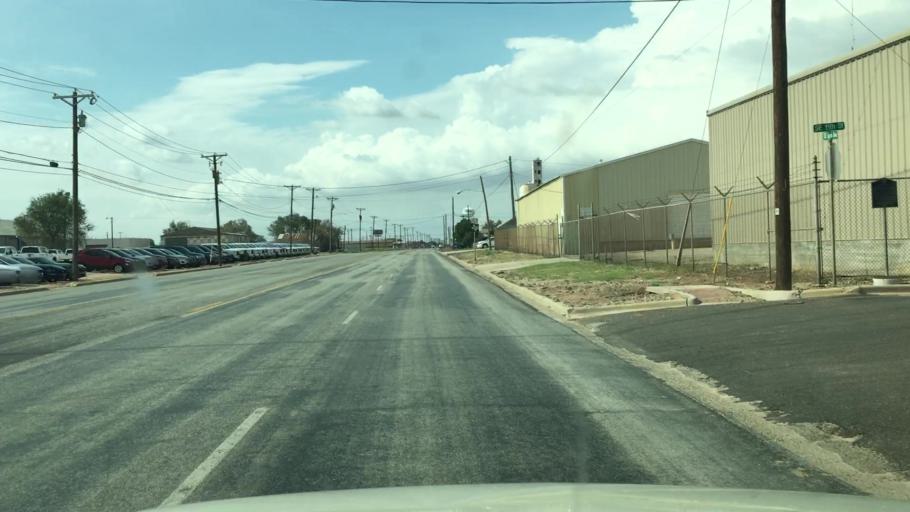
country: US
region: Texas
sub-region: Dawson County
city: Lamesa
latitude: 32.7222
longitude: -101.9458
